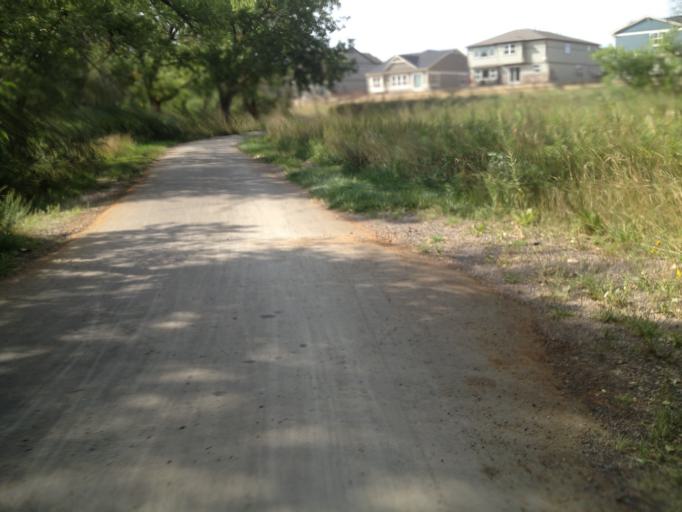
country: US
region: Colorado
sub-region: Boulder County
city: Lafayette
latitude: 39.9797
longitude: -105.1029
